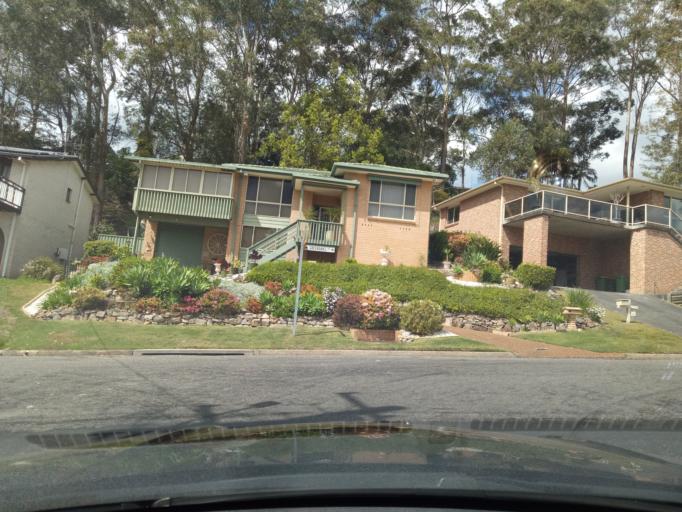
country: AU
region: New South Wales
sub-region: Gosford Shire
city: Narara
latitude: -33.3928
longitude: 151.3548
